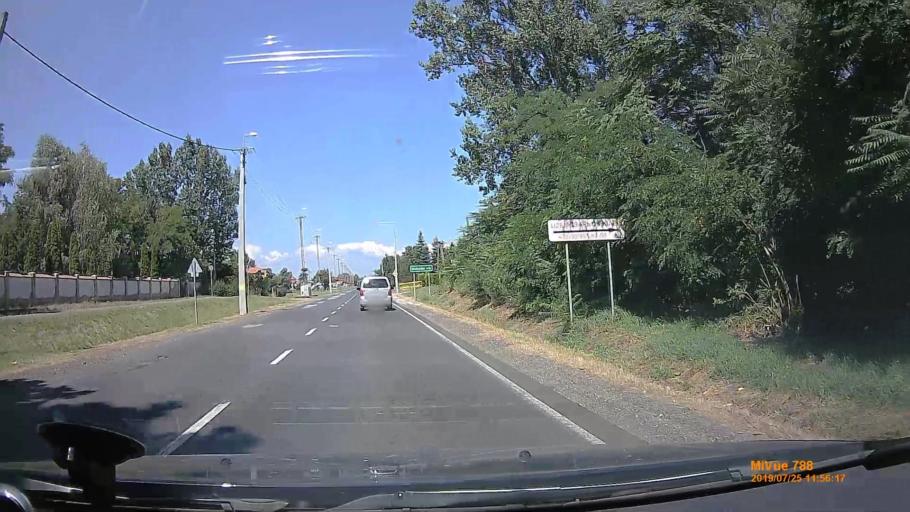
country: HU
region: Szabolcs-Szatmar-Bereg
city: Nyirtelek
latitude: 48.0051
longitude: 21.6396
